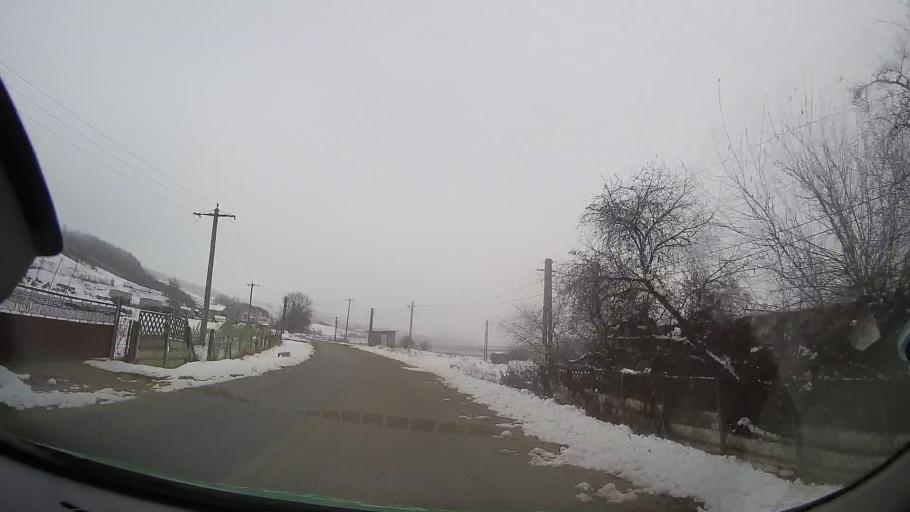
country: RO
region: Bacau
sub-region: Comuna Vultureni
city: Vultureni
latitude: 46.3689
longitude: 27.2827
